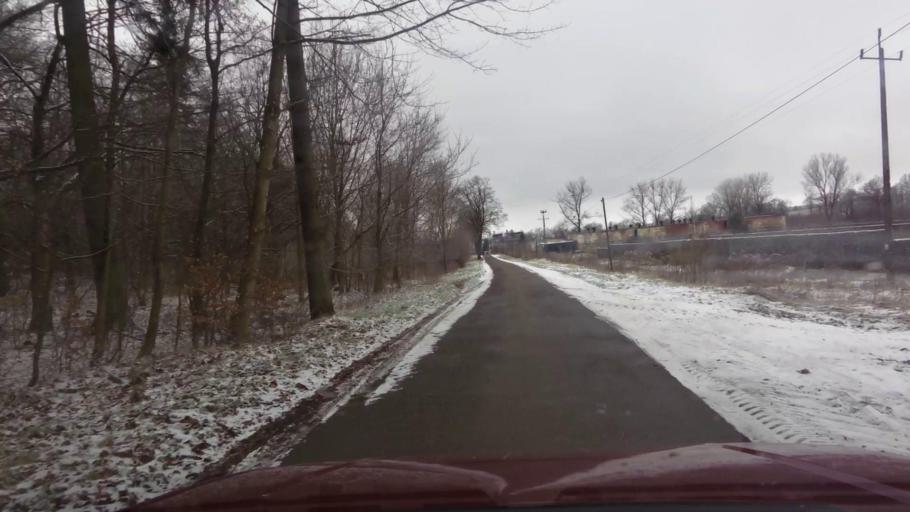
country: PL
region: West Pomeranian Voivodeship
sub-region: Powiat swidwinski
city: Polczyn-Zdroj
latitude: 53.7869
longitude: 16.0417
